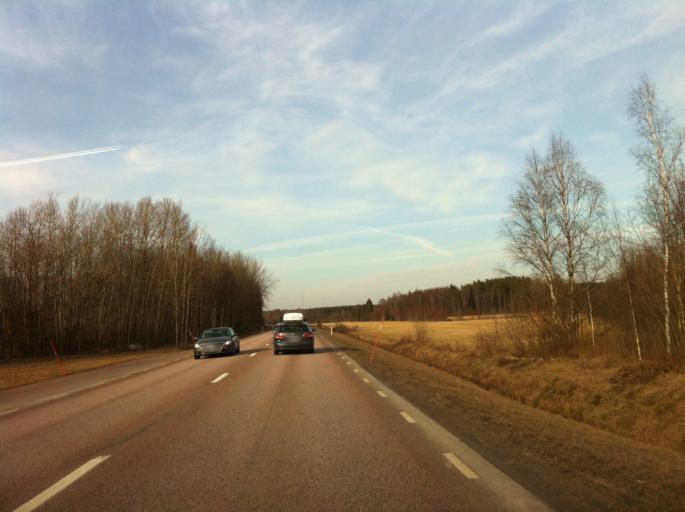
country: SE
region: Vaermland
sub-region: Kristinehamns Kommun
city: Bjorneborg
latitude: 59.2112
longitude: 14.1835
